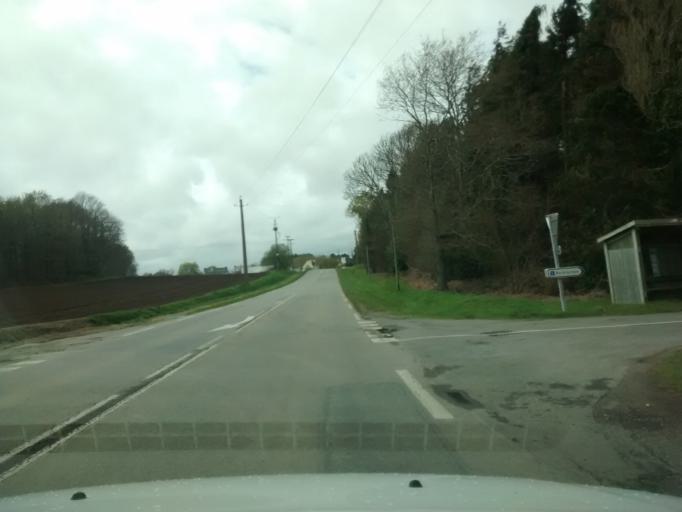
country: FR
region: Brittany
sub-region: Departement du Morbihan
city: Gestel
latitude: 47.7972
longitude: -3.4723
